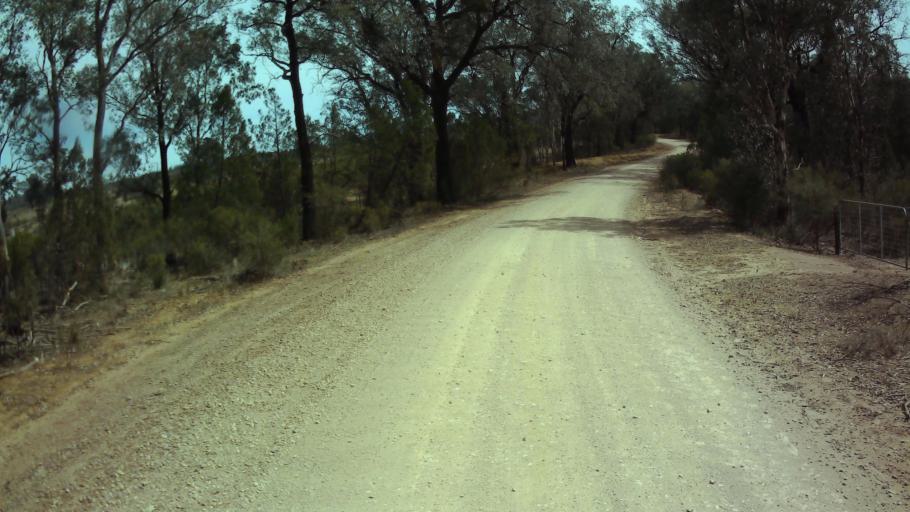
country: AU
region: New South Wales
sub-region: Weddin
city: Grenfell
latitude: -33.9186
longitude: 148.4130
